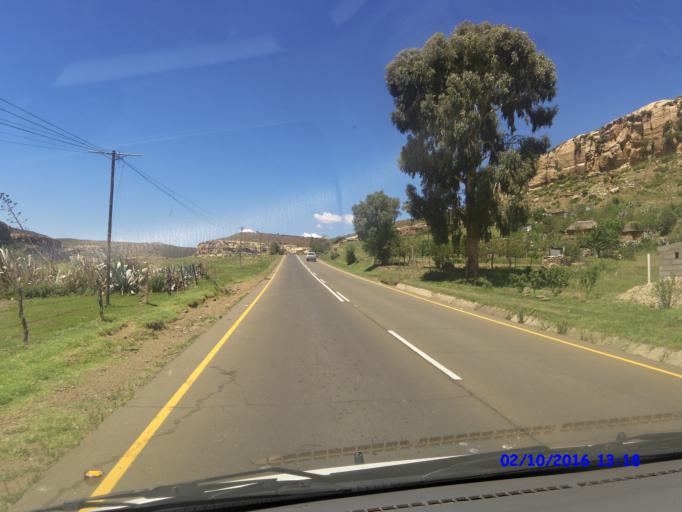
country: LS
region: Maseru
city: Nako
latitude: -29.4236
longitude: 27.6855
